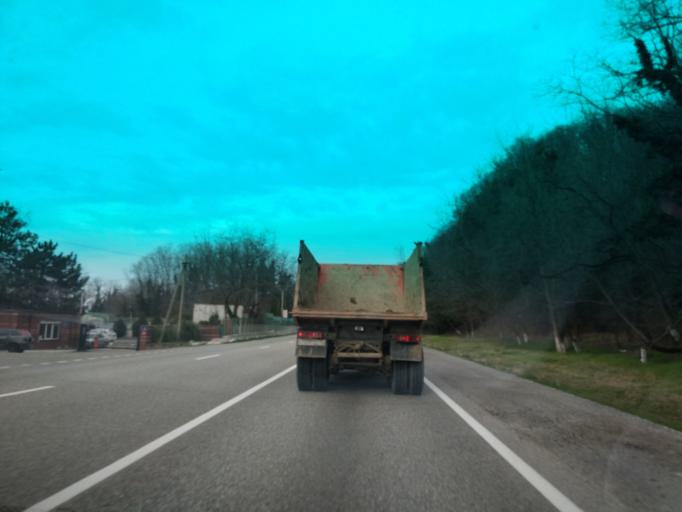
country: RU
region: Krasnodarskiy
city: Nebug
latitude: 44.1693
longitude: 38.9855
